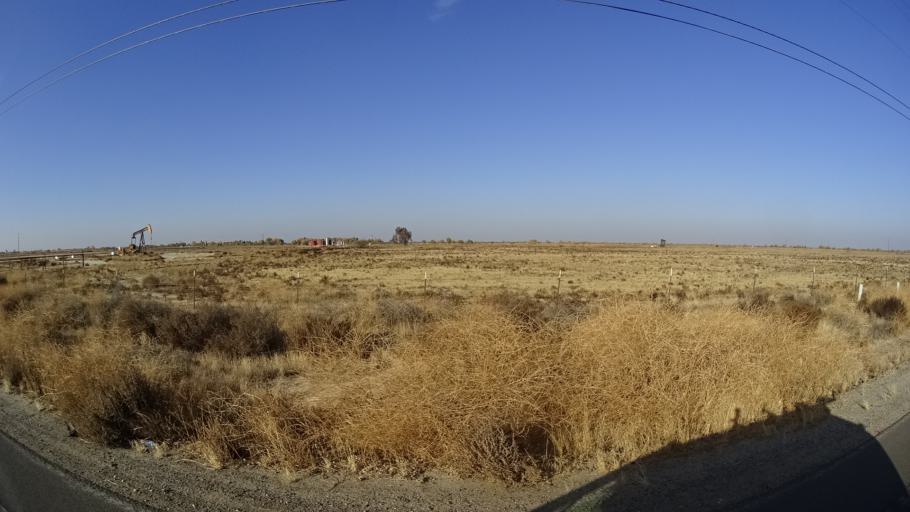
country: US
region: California
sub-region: Kern County
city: Rosedale
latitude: 35.2961
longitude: -119.2376
